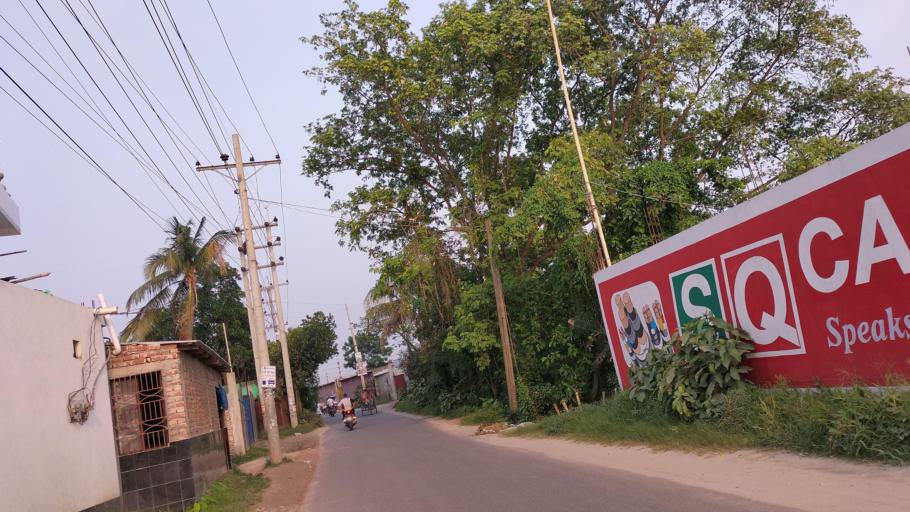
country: BD
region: Dhaka
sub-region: Dhaka
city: Dhaka
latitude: 23.6527
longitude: 90.3486
